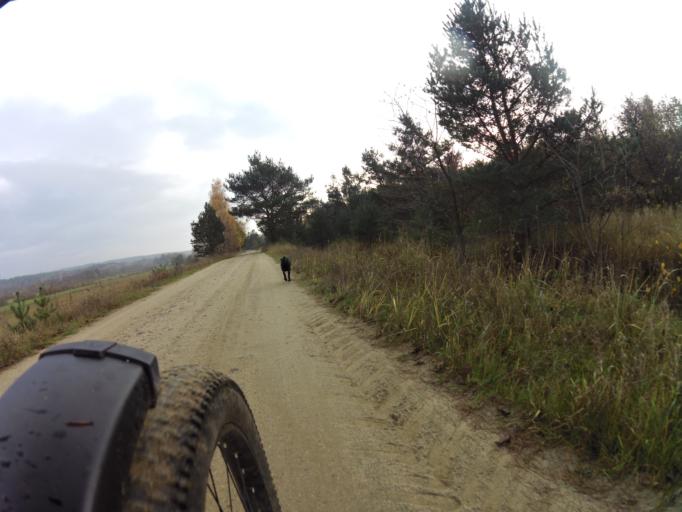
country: PL
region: Pomeranian Voivodeship
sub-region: Powiat wejherowski
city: Gniewino
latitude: 54.7049
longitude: 18.1044
